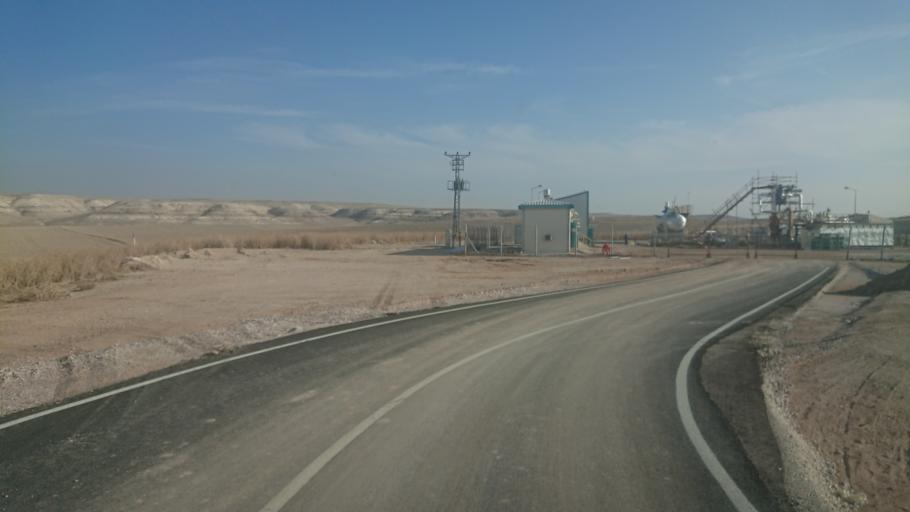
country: TR
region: Aksaray
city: Sultanhani
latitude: 38.0888
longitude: 33.6149
